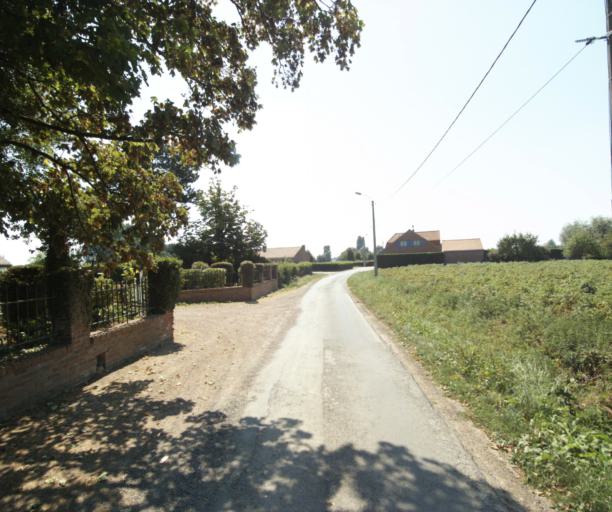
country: FR
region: Nord-Pas-de-Calais
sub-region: Departement du Nord
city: Wervicq-Sud
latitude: 50.7463
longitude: 3.0365
